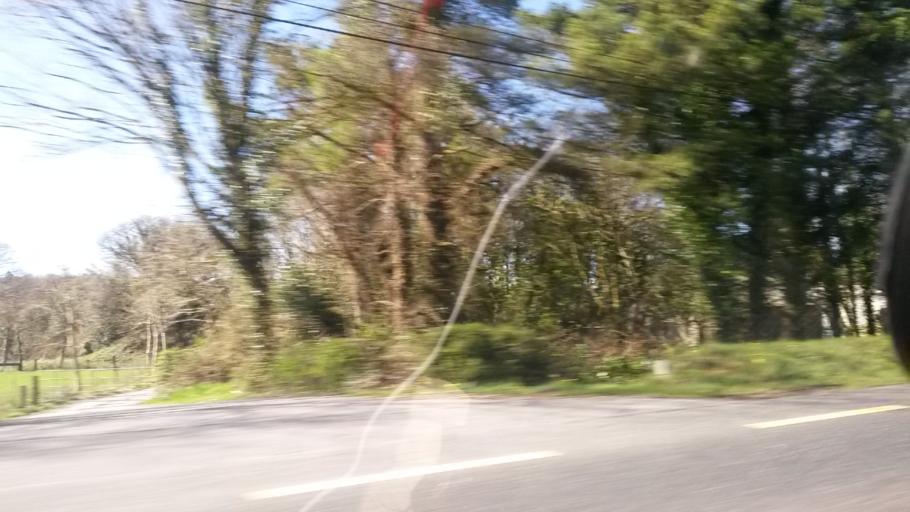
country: IE
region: Munster
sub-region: County Cork
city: Macroom
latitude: 51.9061
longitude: -9.0044
